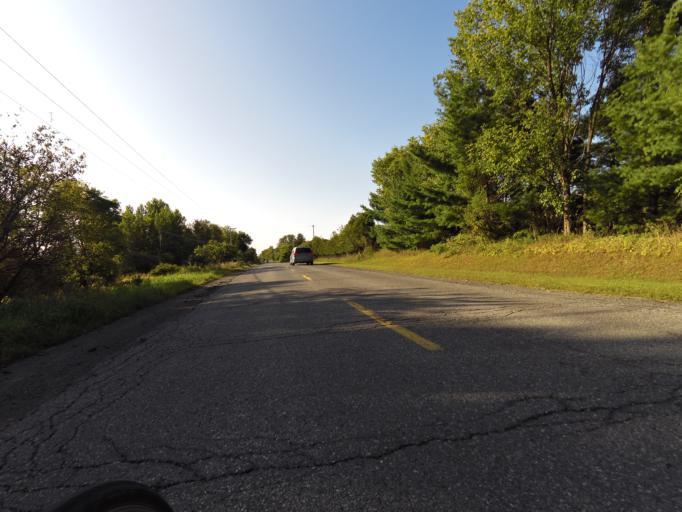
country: CA
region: Ontario
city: Bells Corners
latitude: 45.4655
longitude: -76.0268
